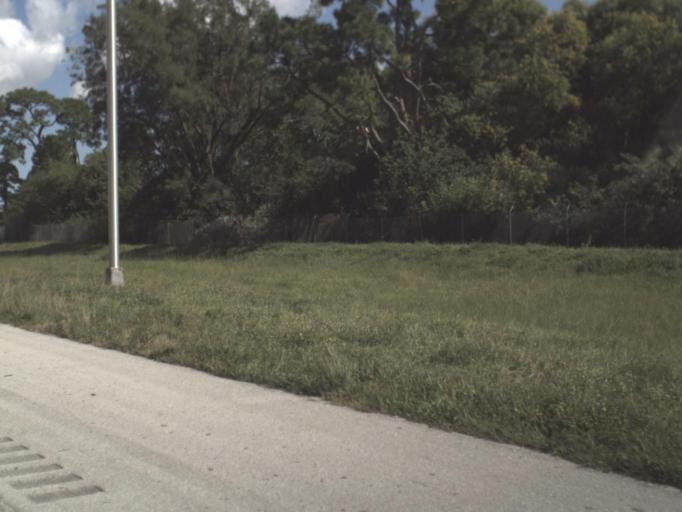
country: US
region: Florida
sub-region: Palm Beach County
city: Villages of Oriole
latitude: 26.4752
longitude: -80.1736
